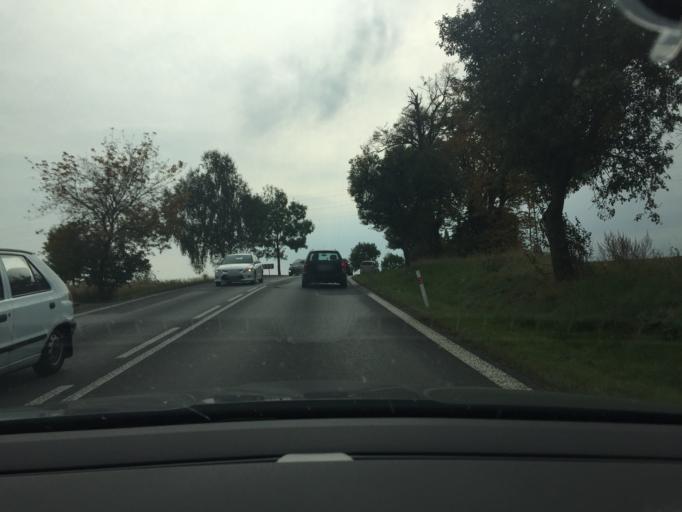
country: CZ
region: Jihocesky
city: Mirovice
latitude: 49.5533
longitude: 14.0825
